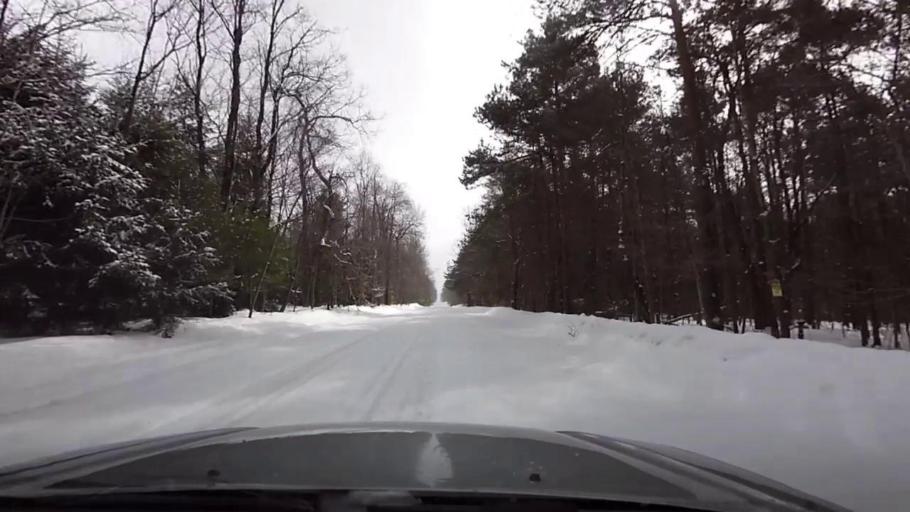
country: US
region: New York
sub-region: Cattaraugus County
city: Franklinville
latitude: 42.3380
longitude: -78.3637
